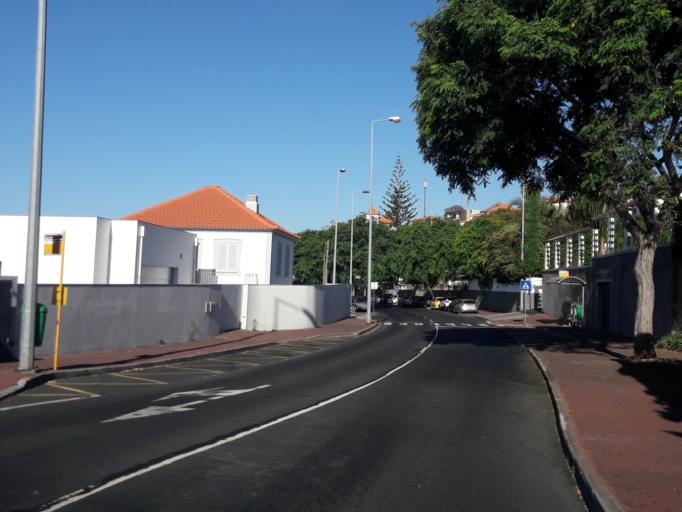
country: PT
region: Madeira
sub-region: Funchal
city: Funchal
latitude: 32.6481
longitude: -16.8904
